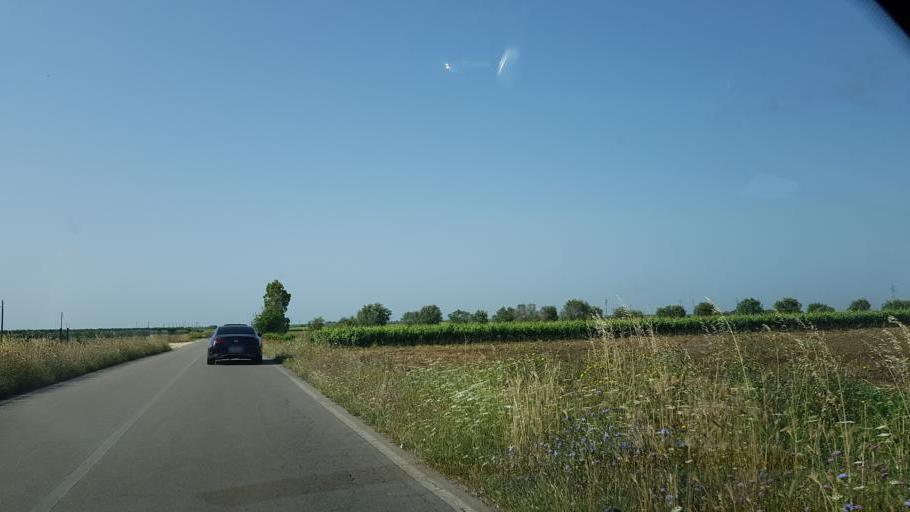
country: IT
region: Apulia
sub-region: Provincia di Brindisi
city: San Pancrazio Salentino
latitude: 40.3839
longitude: 17.8365
